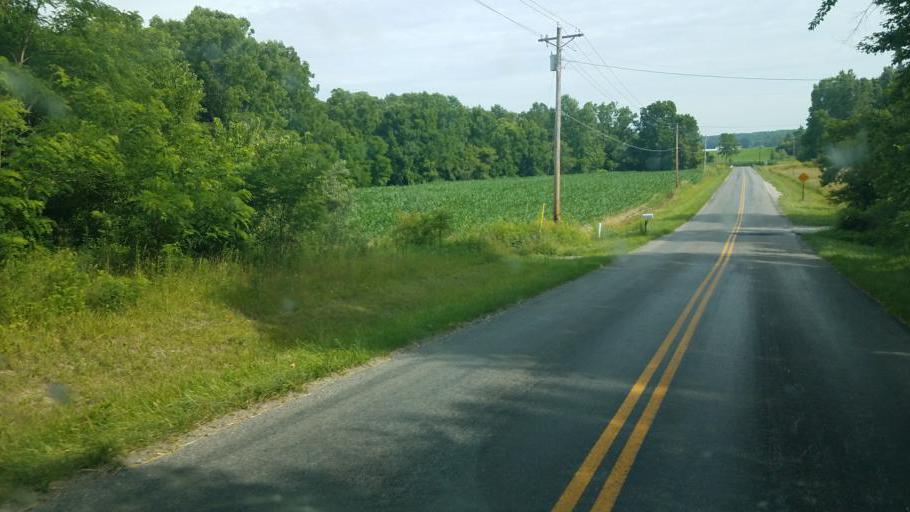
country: US
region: Ohio
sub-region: Medina County
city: Lodi
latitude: 41.0478
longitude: -82.0344
